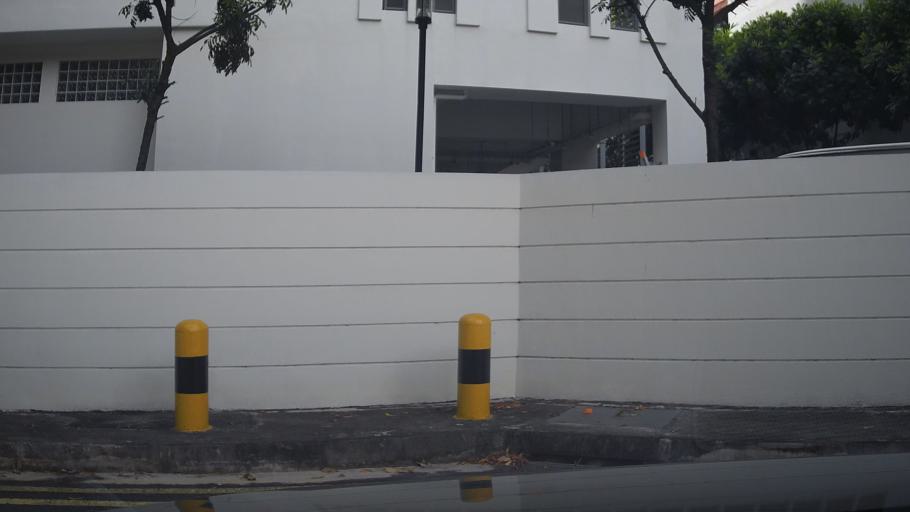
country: SG
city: Singapore
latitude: 1.3101
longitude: 103.8965
